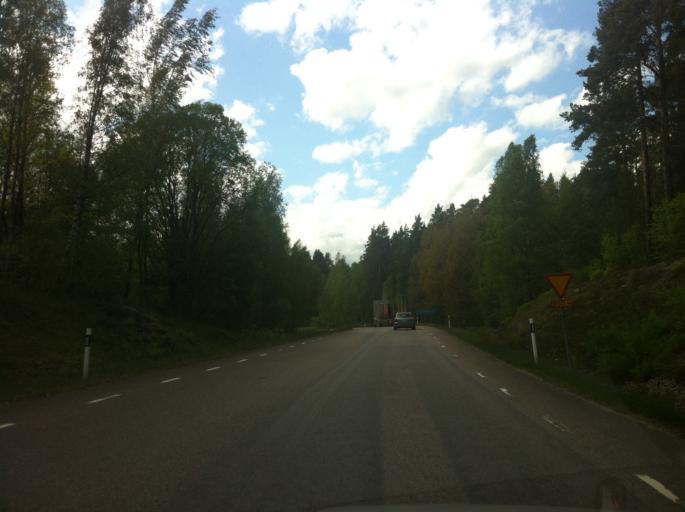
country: SE
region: Vaermland
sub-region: Kristinehamns Kommun
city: Kristinehamn
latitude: 59.3190
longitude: 14.1418
